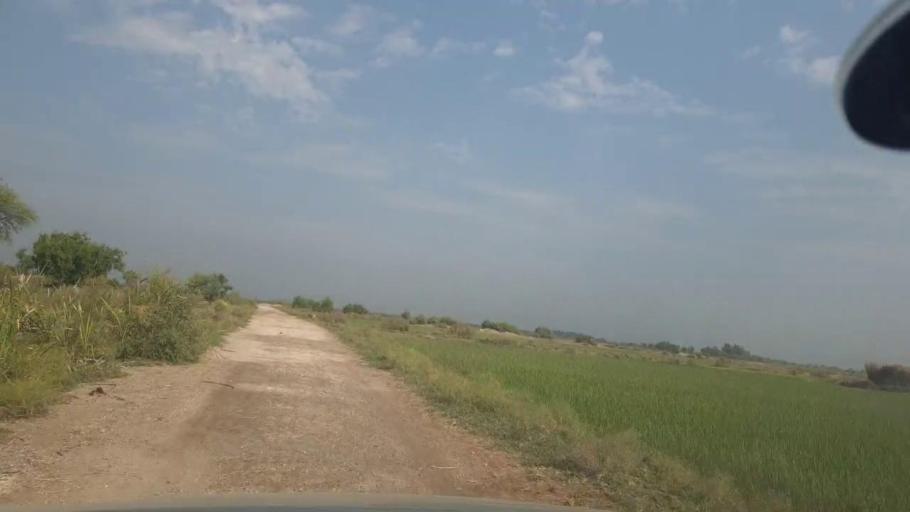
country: PK
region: Balochistan
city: Mehrabpur
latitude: 28.0351
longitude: 68.1280
